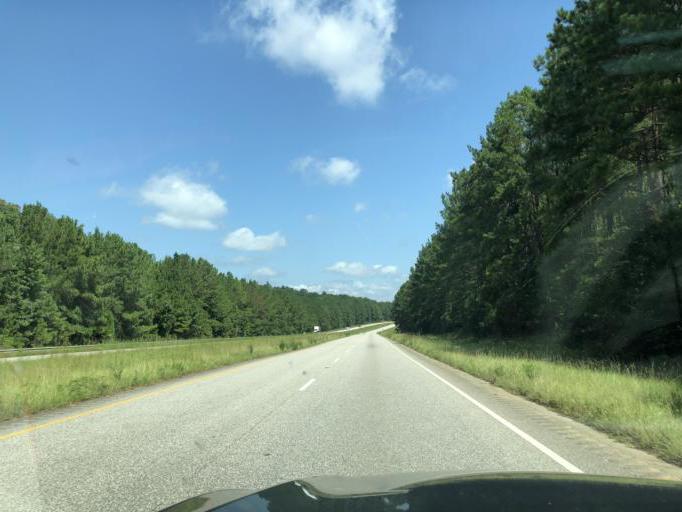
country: US
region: Alabama
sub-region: Henry County
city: Abbeville
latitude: 31.7334
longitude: -85.2536
